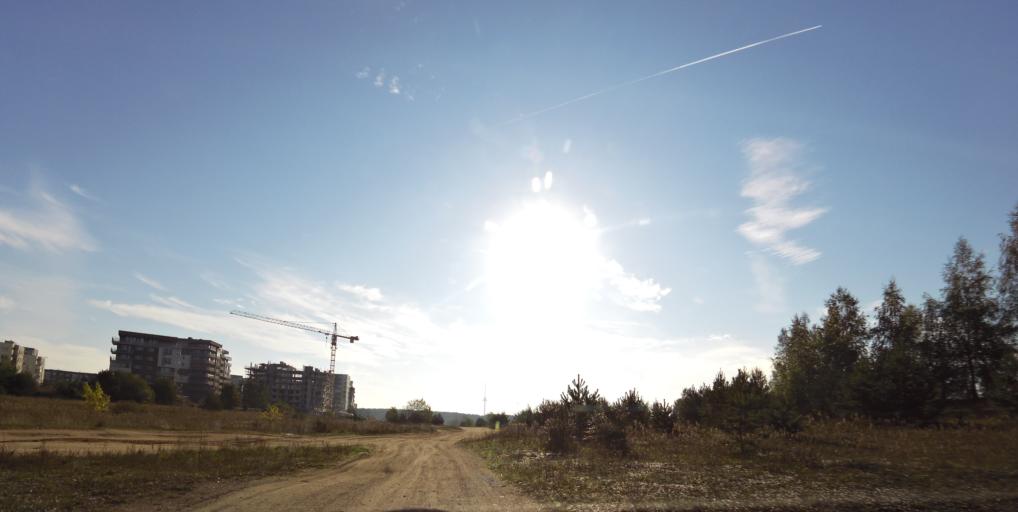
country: LT
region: Vilnius County
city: Pilaite
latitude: 54.7048
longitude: 25.1696
